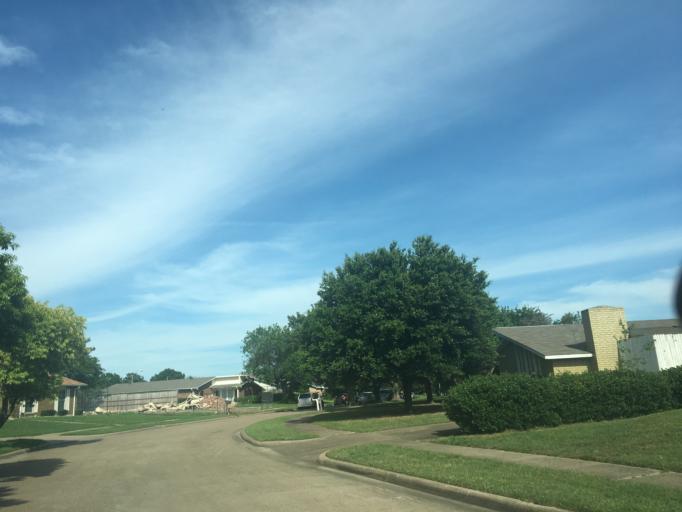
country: US
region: Texas
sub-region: Dallas County
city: Richardson
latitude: 32.9338
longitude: -96.7122
